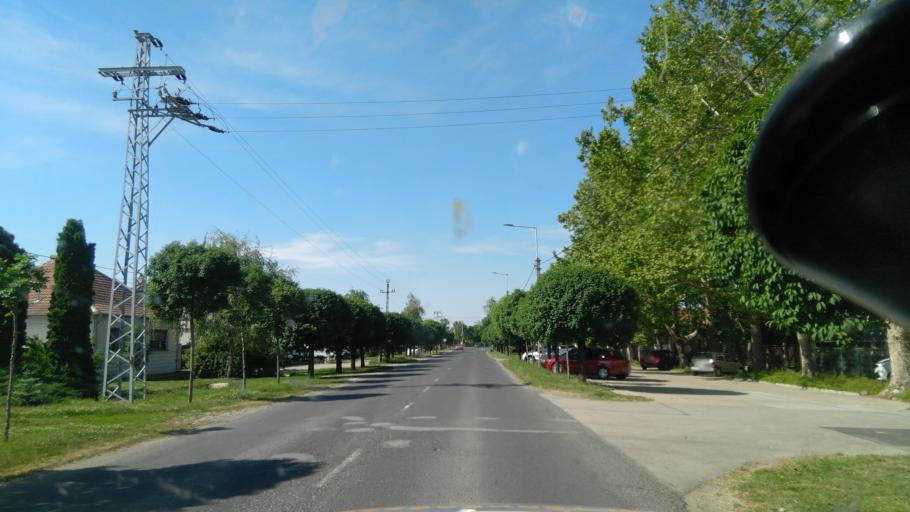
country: HU
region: Bekes
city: Gyula
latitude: 46.6519
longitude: 21.2834
